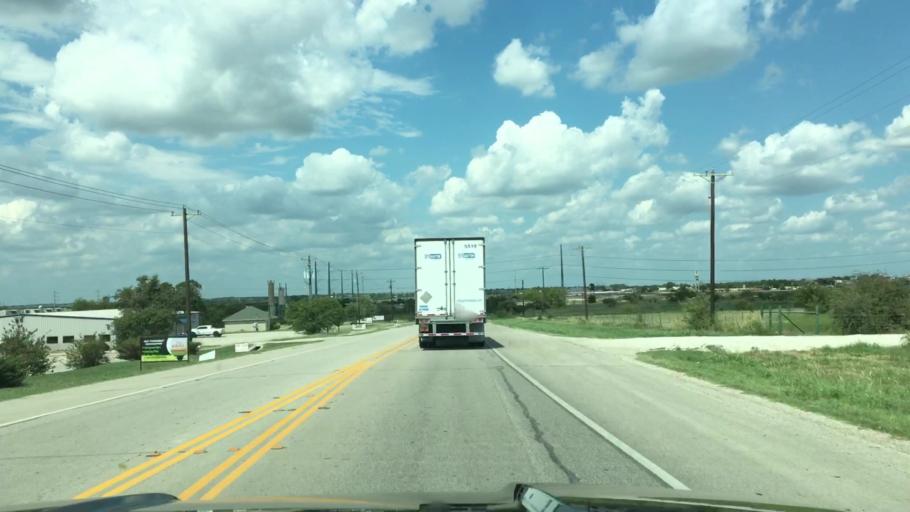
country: US
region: Texas
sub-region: Tarrant County
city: Pecan Acres
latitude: 32.9581
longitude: -97.4208
